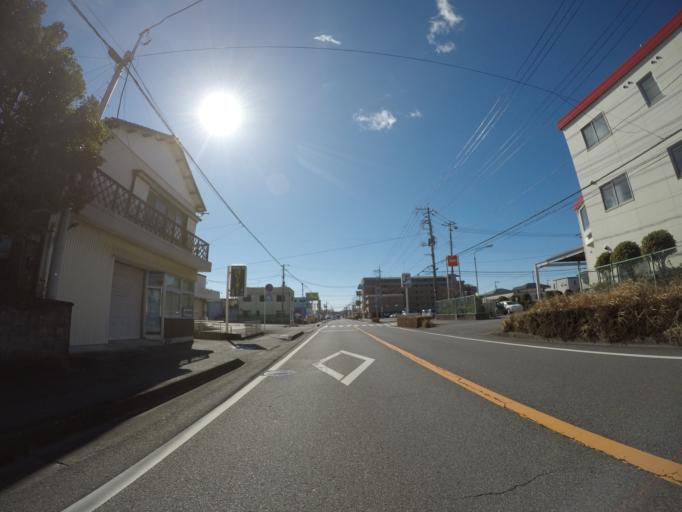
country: JP
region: Shizuoka
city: Numazu
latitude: 35.1327
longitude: 138.8027
